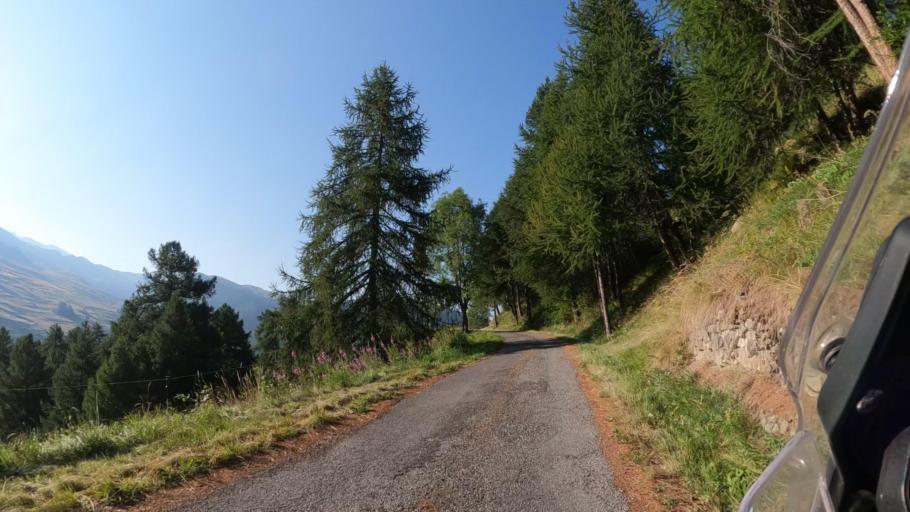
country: FR
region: Provence-Alpes-Cote d'Azur
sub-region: Departement des Hautes-Alpes
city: Guillestre
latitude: 44.6001
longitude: 6.6824
